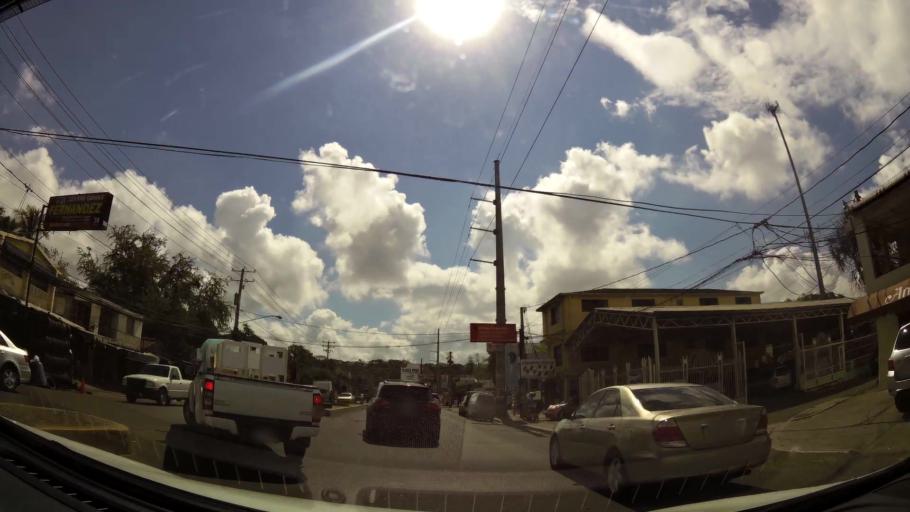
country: DO
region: Santiago
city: Santiago de los Caballeros
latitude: 19.4705
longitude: -70.6898
